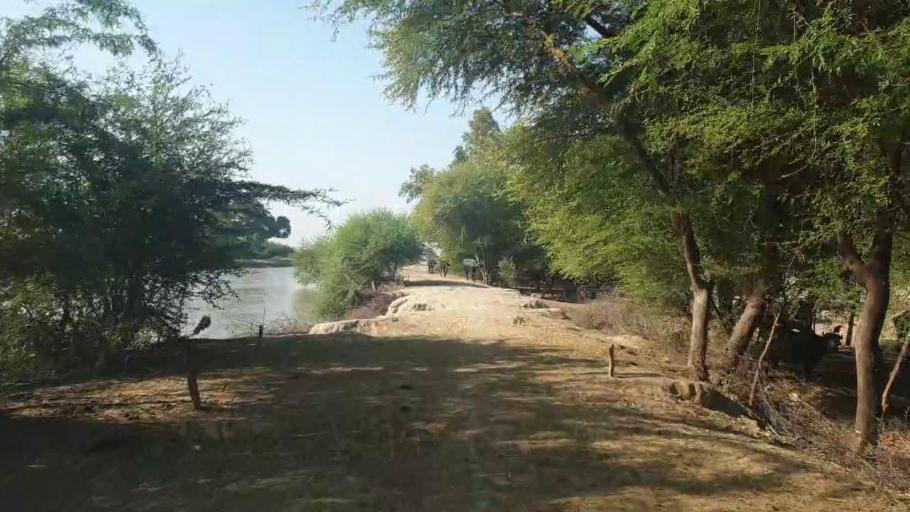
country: PK
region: Sindh
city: Badin
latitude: 24.7020
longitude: 68.8812
